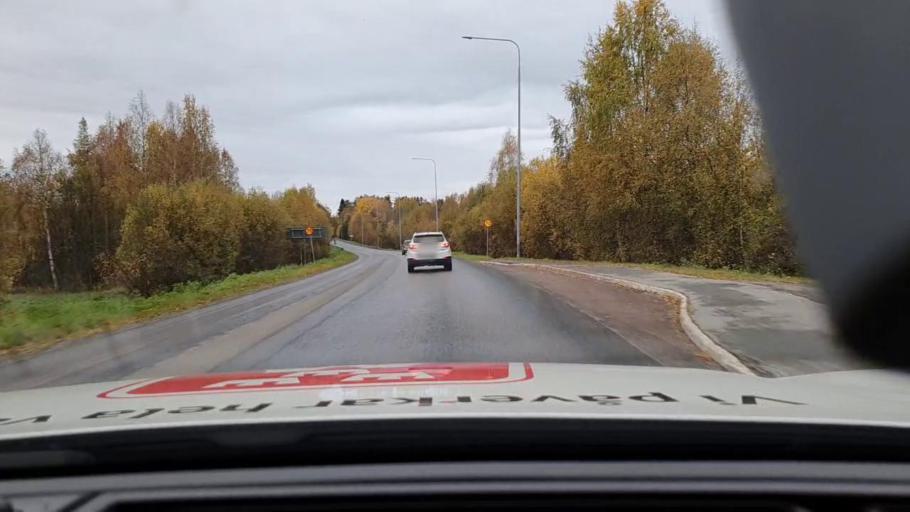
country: SE
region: Norrbotten
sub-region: Bodens Kommun
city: Saevast
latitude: 65.7677
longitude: 21.7399
